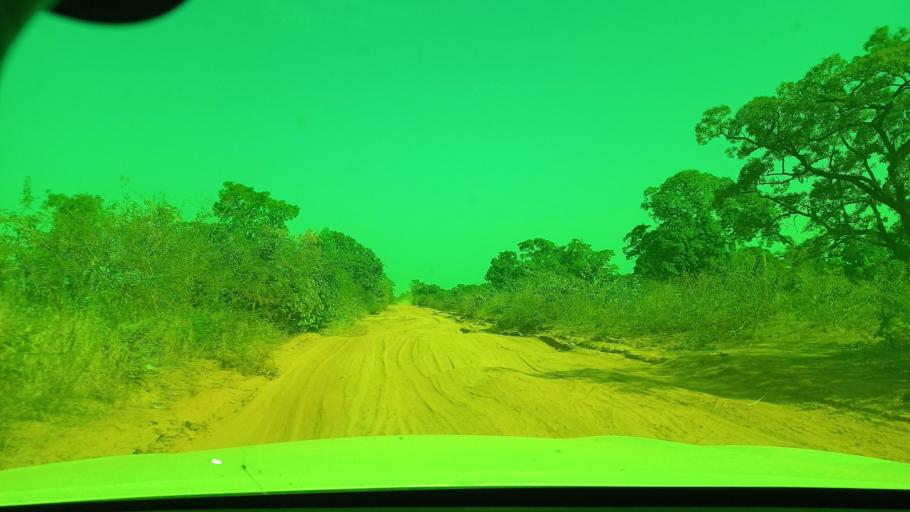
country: ML
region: Bamako
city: Bamako
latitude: 12.3972
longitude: -7.9903
